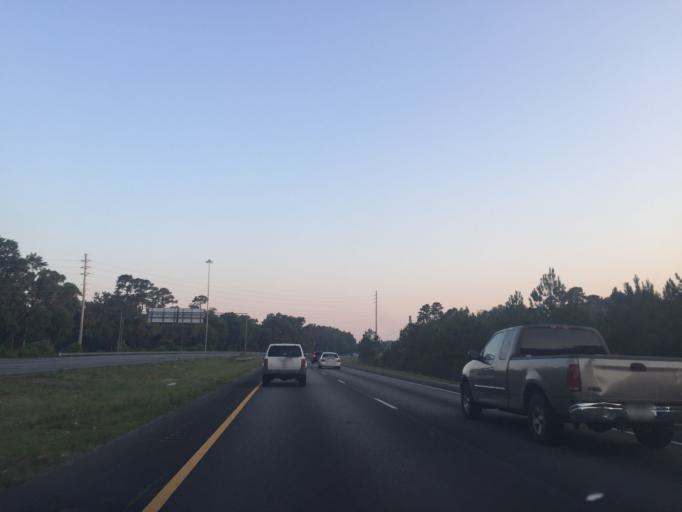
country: US
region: Georgia
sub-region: Chatham County
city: Isle of Hope
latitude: 32.0086
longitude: -81.0804
